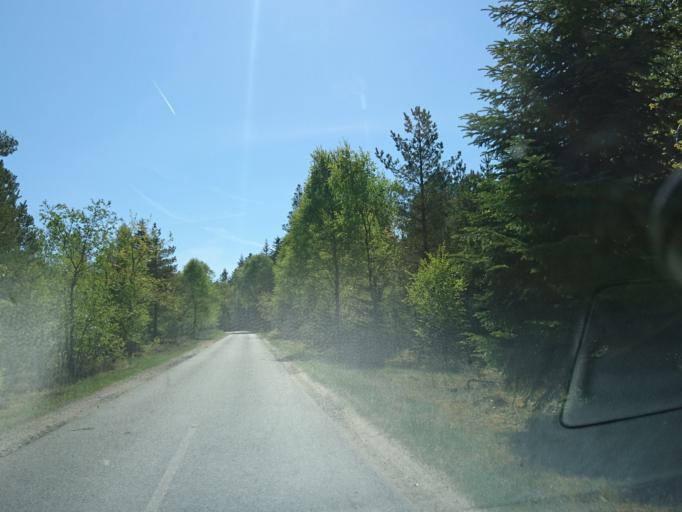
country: DK
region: North Denmark
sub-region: Hjorring Kommune
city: Sindal
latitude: 57.5957
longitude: 10.2290
